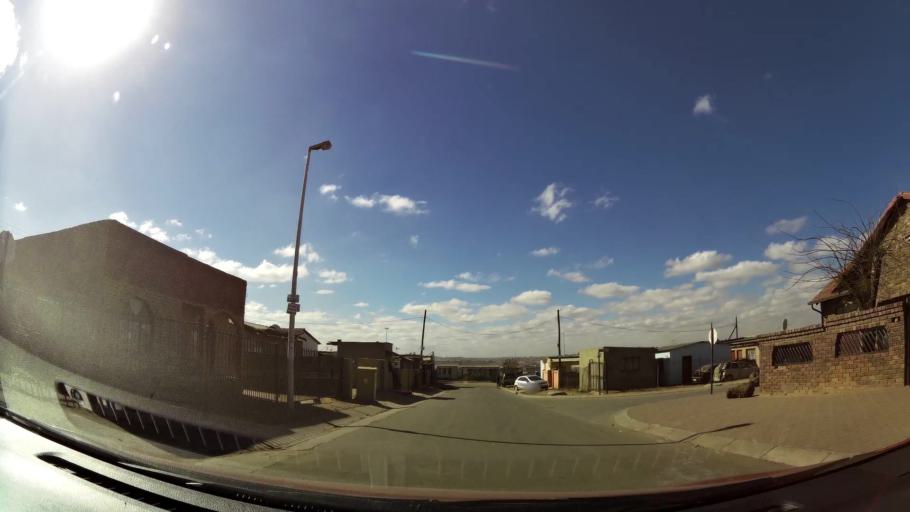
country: ZA
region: Gauteng
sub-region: City of Johannesburg Metropolitan Municipality
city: Modderfontein
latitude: -26.0366
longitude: 28.1791
